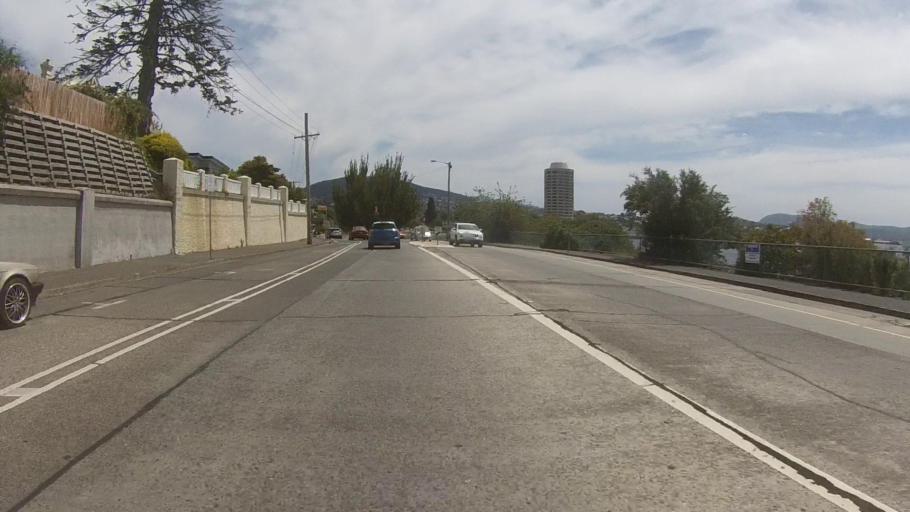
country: AU
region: Tasmania
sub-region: Hobart
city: Sandy Bay
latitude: -42.9063
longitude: 147.3415
